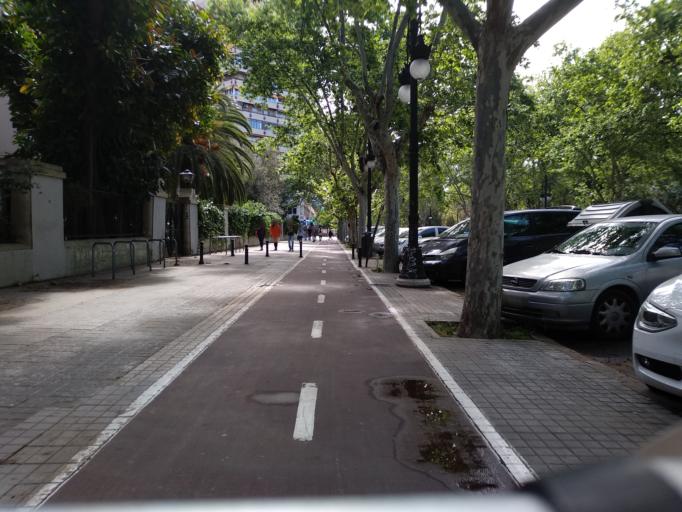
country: ES
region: Valencia
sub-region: Provincia de Valencia
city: Valencia
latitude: 39.4777
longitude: -0.3591
